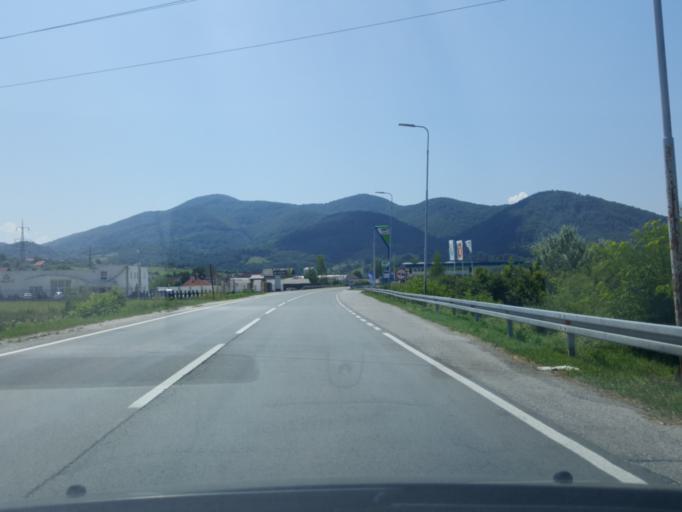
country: RS
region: Central Serbia
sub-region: Moravicki Okrug
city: Gornji Milanovac
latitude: 44.0128
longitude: 20.4634
